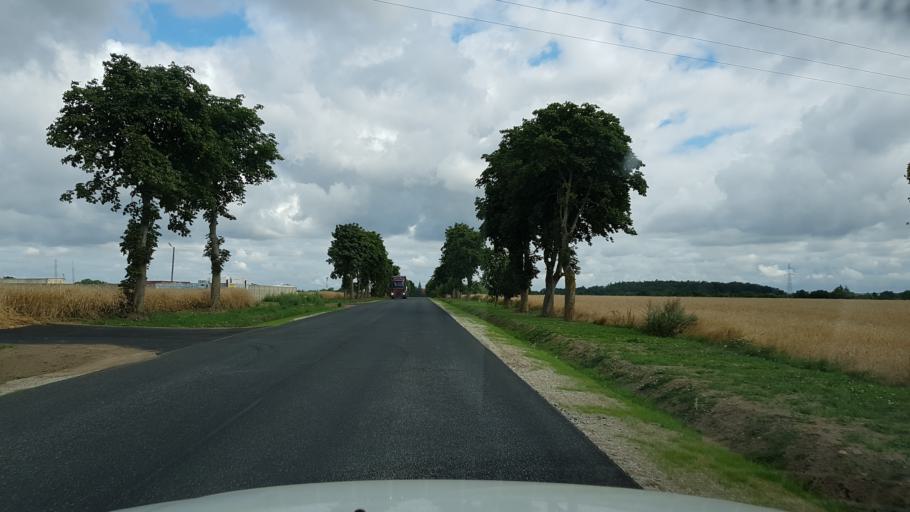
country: PL
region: West Pomeranian Voivodeship
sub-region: Powiat gryficki
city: Gryfice
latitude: 53.8965
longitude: 15.2054
